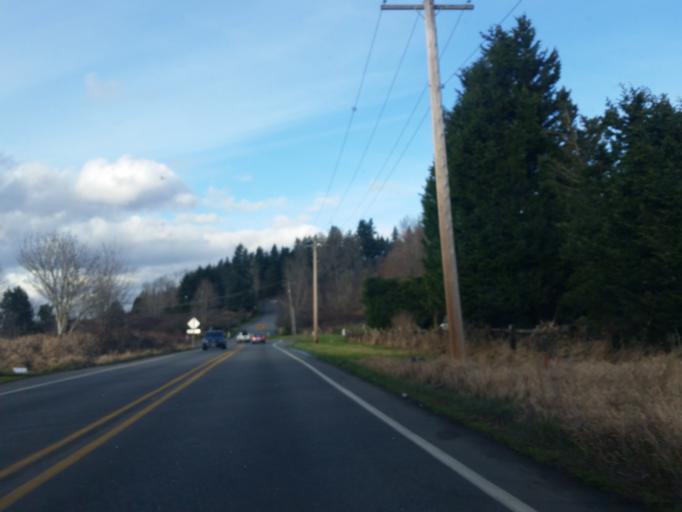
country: US
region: Washington
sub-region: King County
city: Redmond
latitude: 47.7134
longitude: -122.1317
